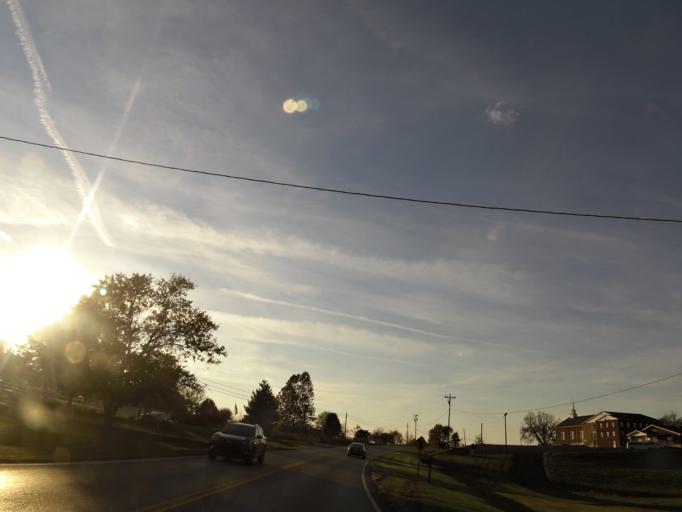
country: US
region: Kentucky
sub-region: Garrard County
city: Lancaster
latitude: 37.6739
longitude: -84.6427
